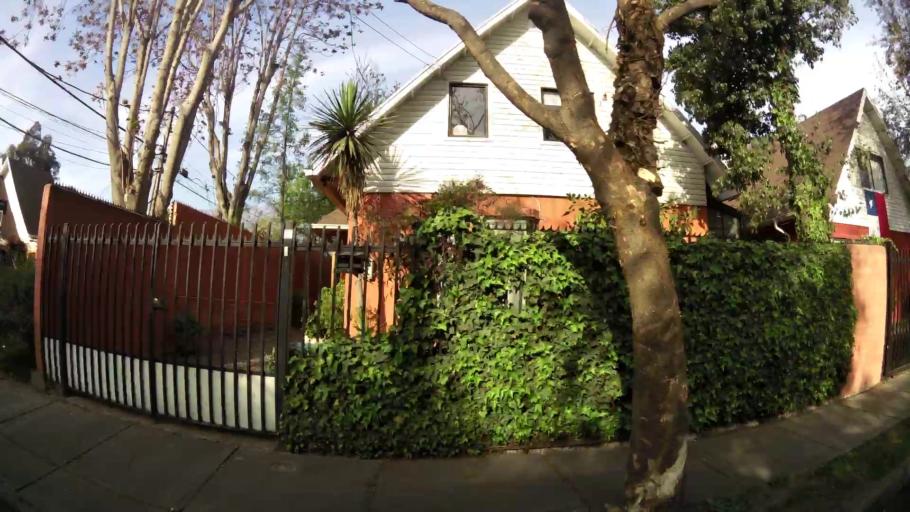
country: CL
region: Santiago Metropolitan
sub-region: Provincia de Santiago
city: Villa Presidente Frei, Nunoa, Santiago, Chile
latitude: -33.5077
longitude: -70.5584
